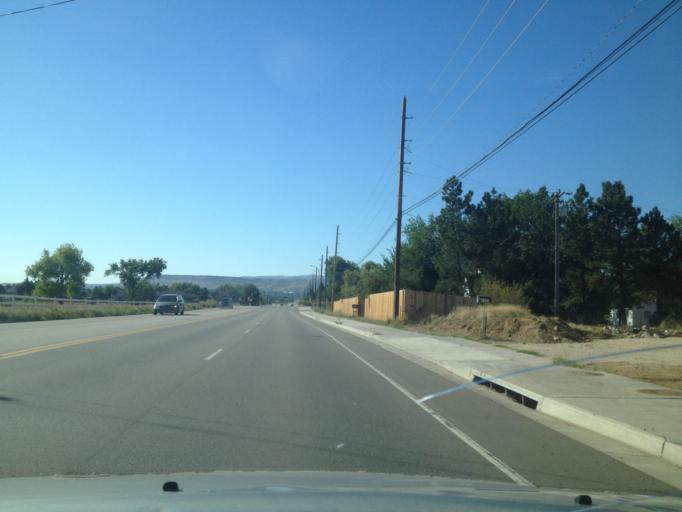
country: US
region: Colorado
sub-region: Jefferson County
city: Applewood
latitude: 39.7937
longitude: -105.1746
